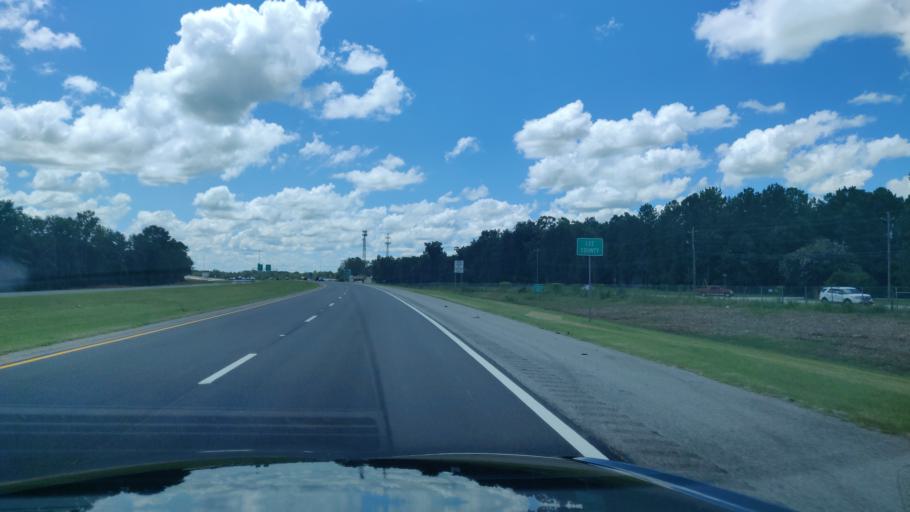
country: US
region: Georgia
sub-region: Dougherty County
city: Albany
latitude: 31.6224
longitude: -84.2208
